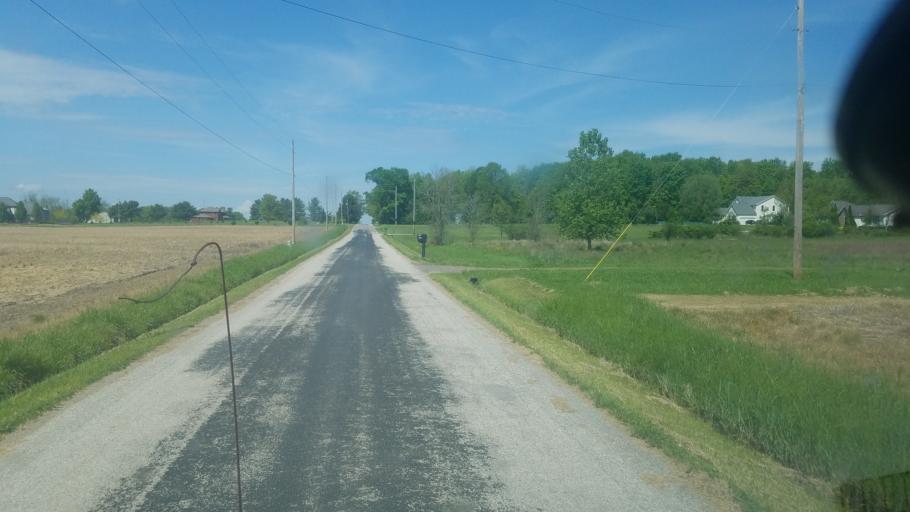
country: US
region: Ohio
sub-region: Richland County
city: Lincoln Heights
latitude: 40.8622
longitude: -82.4669
